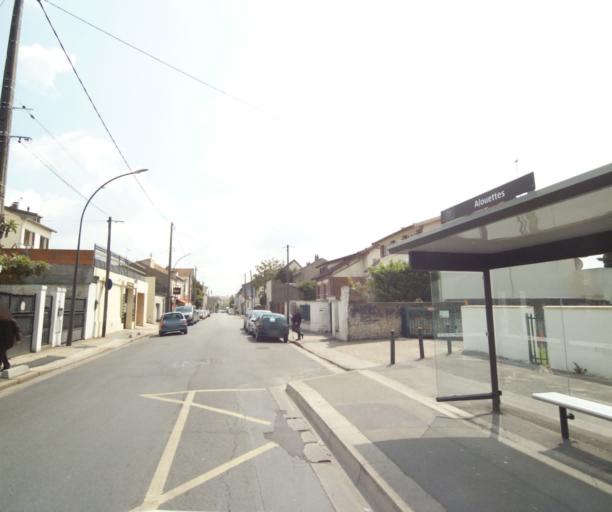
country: FR
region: Ile-de-France
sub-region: Departement du Val-d'Oise
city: Bezons
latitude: 48.9408
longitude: 2.2182
